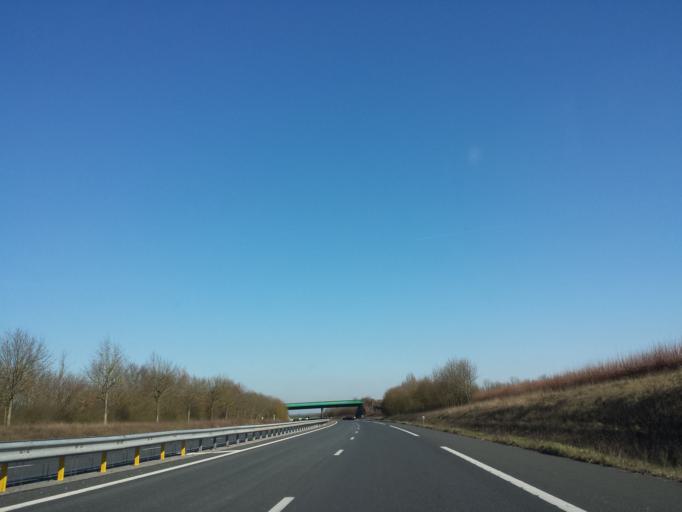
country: FR
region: Picardie
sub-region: Departement de l'Oise
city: Tille
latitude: 49.5133
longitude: 2.1840
